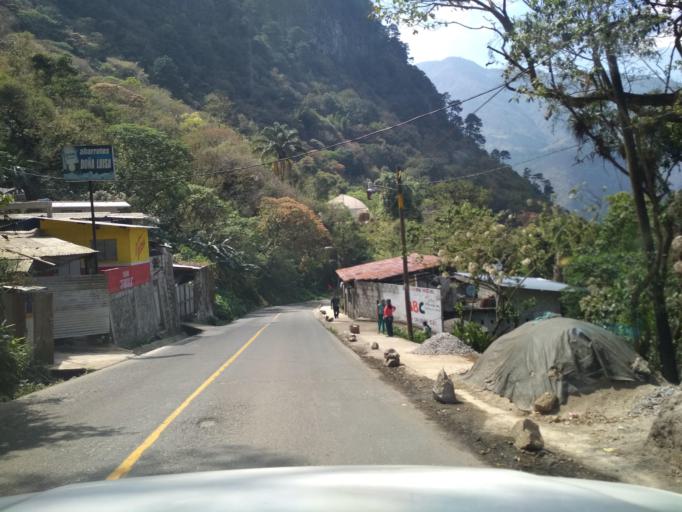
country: MX
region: Veracruz
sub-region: Tlilapan
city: Tonalixco
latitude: 18.7848
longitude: -97.0891
